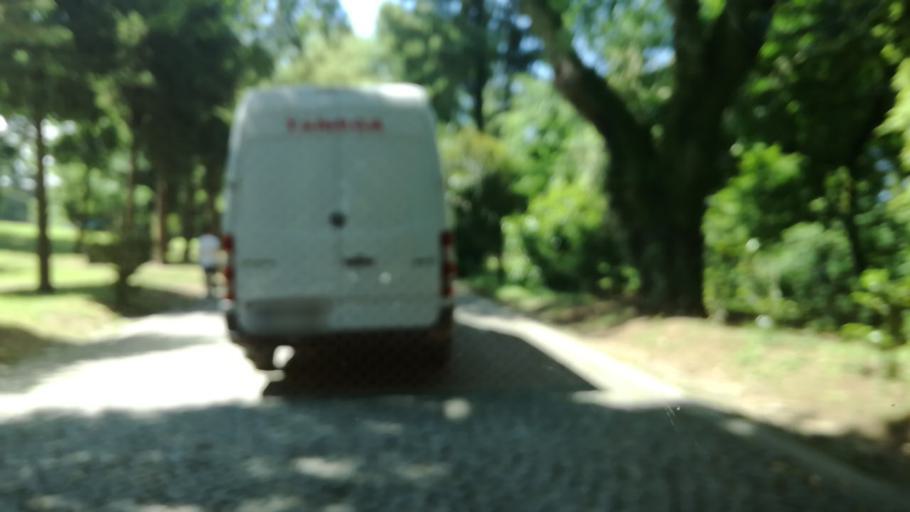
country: PT
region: Braga
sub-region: Braga
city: Adaufe
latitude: 41.5536
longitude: -8.3756
